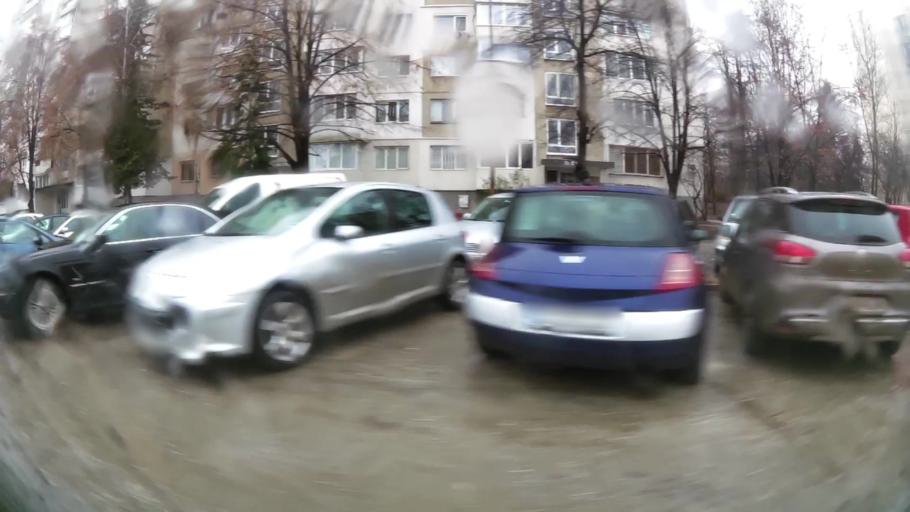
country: BG
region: Sofia-Capital
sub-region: Stolichna Obshtina
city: Sofia
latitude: 42.6569
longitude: 23.3638
